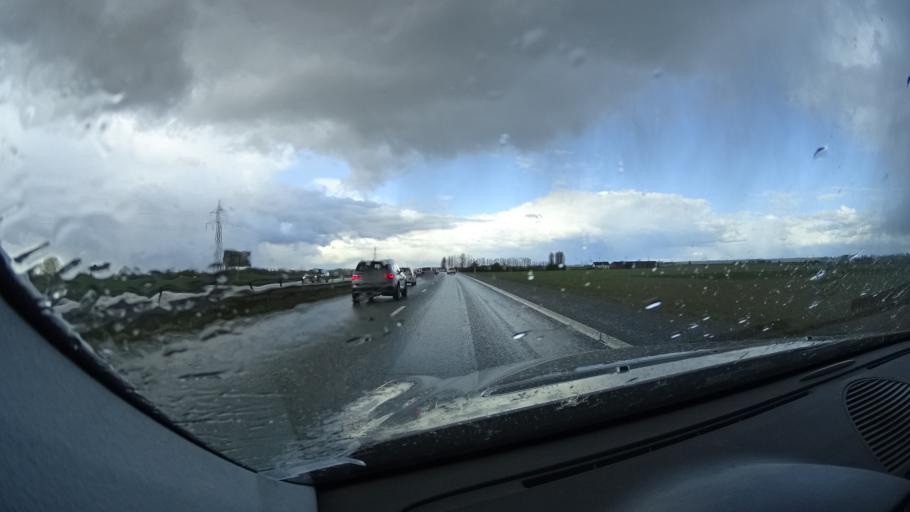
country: SE
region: Skane
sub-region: Lomma Kommun
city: Lomma
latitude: 55.6656
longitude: 13.0999
